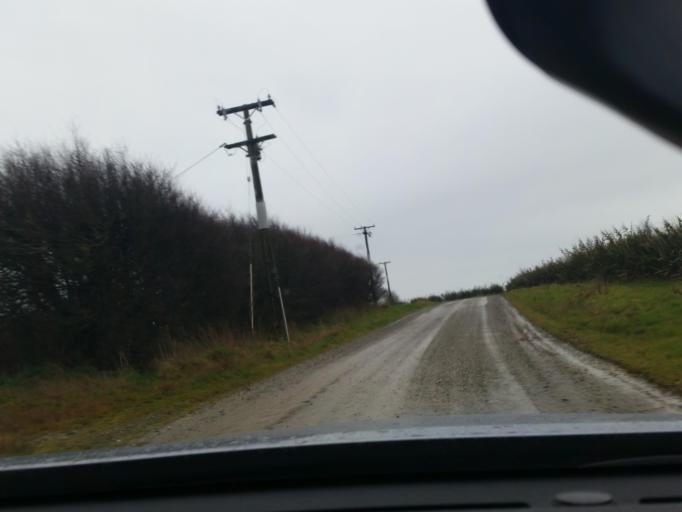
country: NZ
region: Southland
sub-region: Southland District
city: Winton
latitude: -46.2426
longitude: 168.4761
